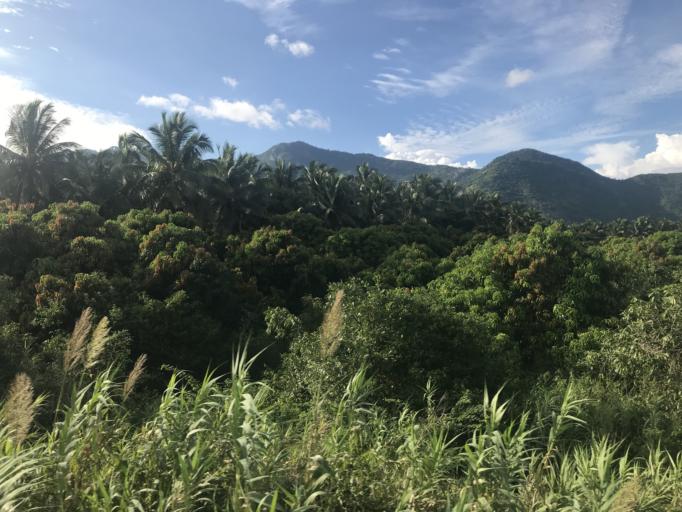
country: IN
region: Tamil Nadu
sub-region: Coimbatore
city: Madukkarai
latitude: 10.8852
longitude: 76.8751
